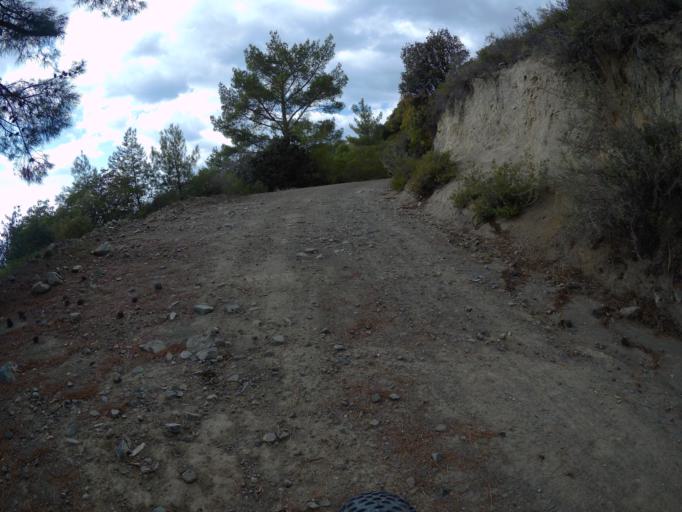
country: CY
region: Lefkosia
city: Kakopetria
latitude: 34.9041
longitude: 32.8316
